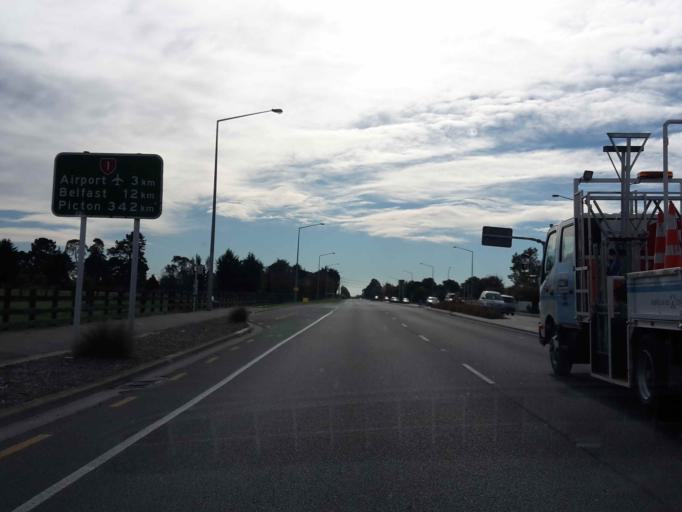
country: NZ
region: Canterbury
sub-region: Selwyn District
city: Prebbleton
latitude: -43.5193
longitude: 172.5346
